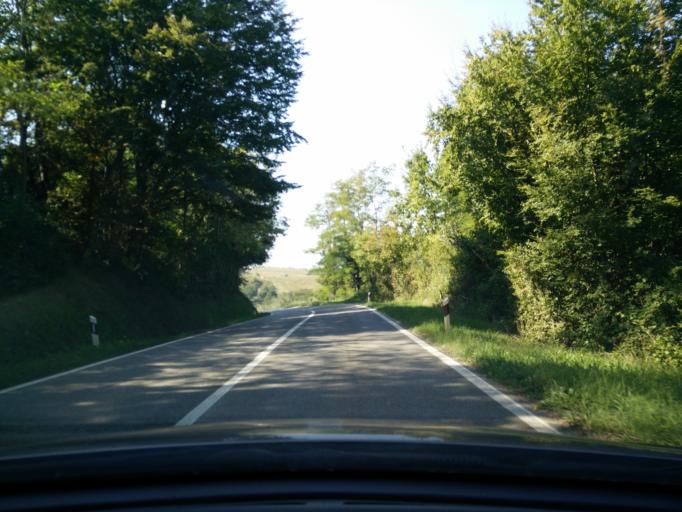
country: HR
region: Istarska
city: Karojba
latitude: 45.3343
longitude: 13.7554
